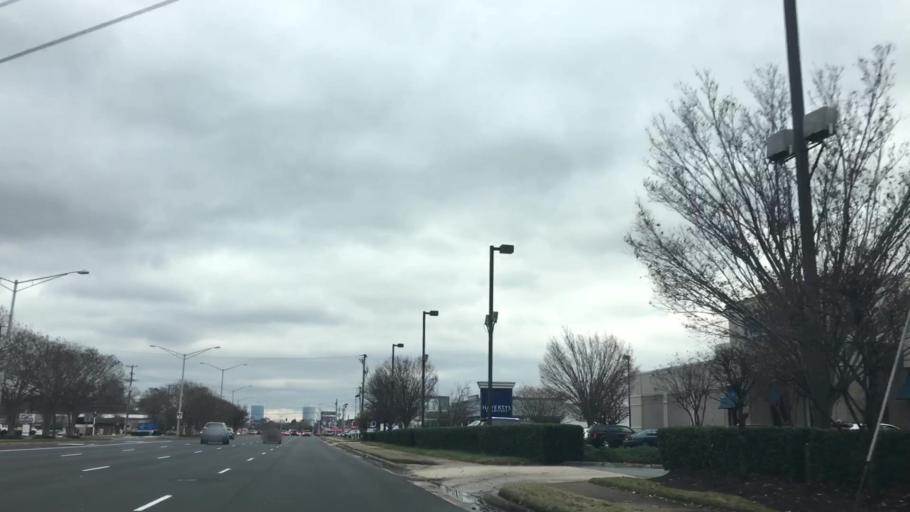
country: US
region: Virginia
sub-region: City of Chesapeake
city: Chesapeake
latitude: 36.8471
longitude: -76.1605
